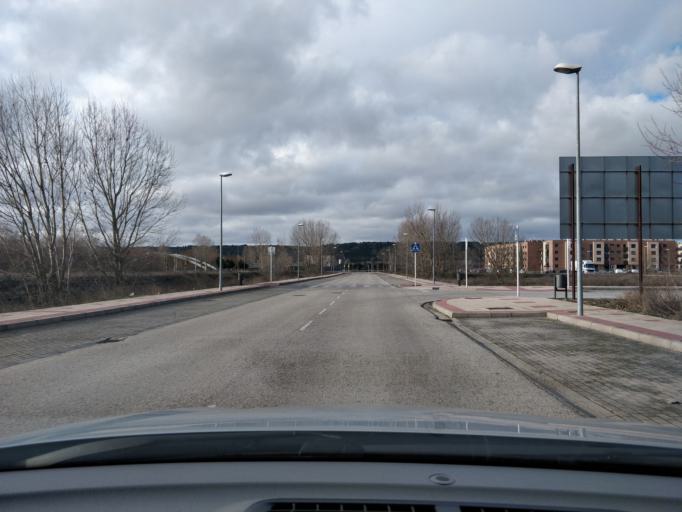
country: ES
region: Castille and Leon
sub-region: Provincia de Burgos
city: Villalbilla de Burgos
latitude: 42.3530
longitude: -3.7589
